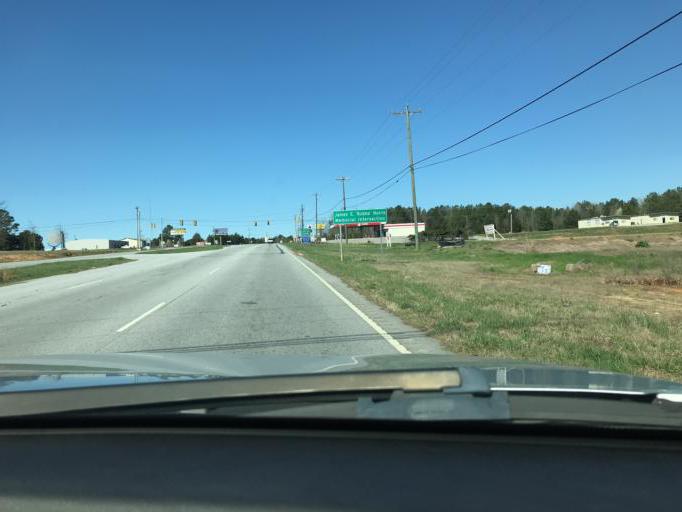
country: US
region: South Carolina
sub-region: Laurens County
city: Watts Mills
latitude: 34.4799
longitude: -81.9427
